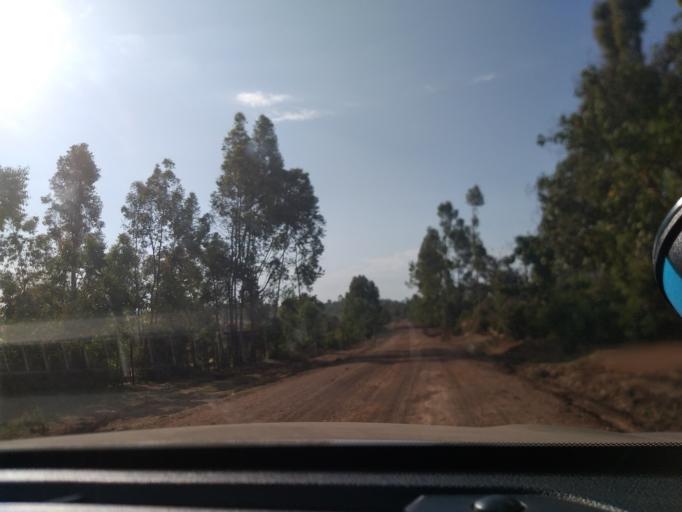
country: ET
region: Oromiya
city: Shashemene
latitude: 7.4285
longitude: 38.8081
